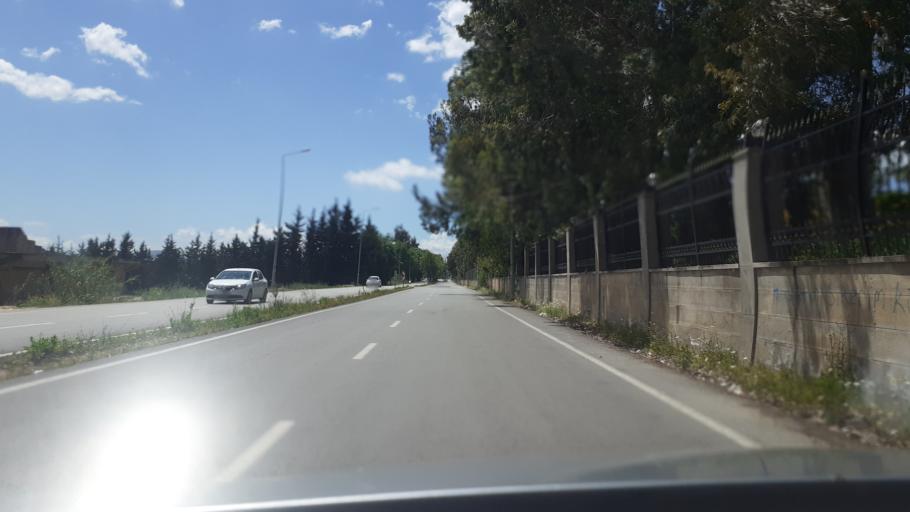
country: TR
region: Hatay
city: Anayazi
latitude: 36.3252
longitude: 36.1984
